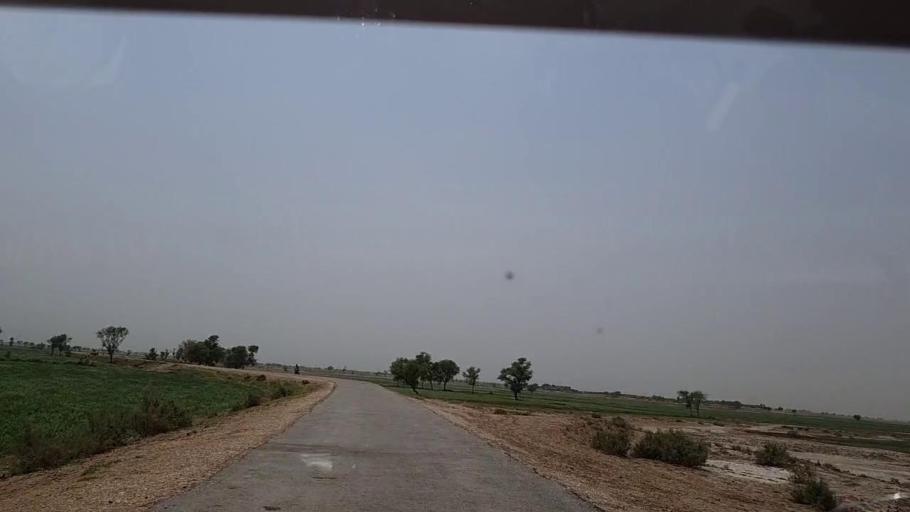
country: PK
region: Sindh
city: Khairpur Nathan Shah
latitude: 27.0218
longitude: 67.6663
